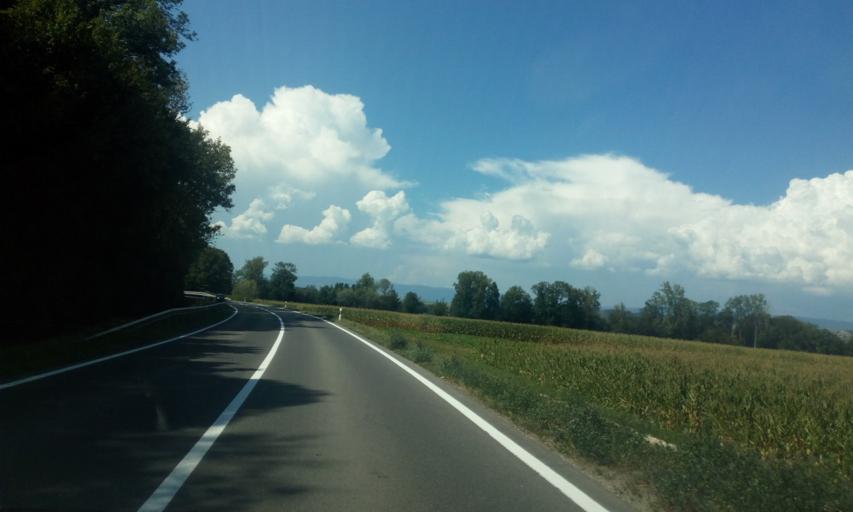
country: CH
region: Fribourg
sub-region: Broye District
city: Domdidier
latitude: 46.8879
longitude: 7.0192
